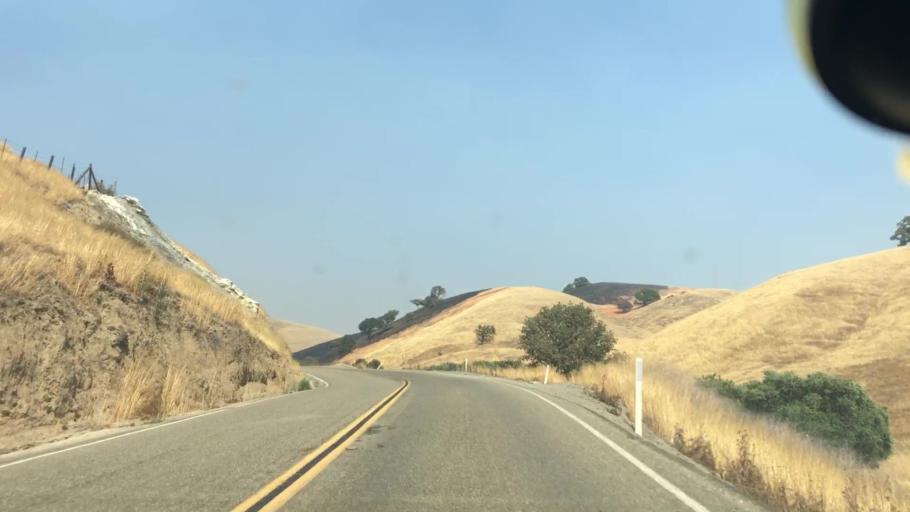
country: US
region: California
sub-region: Alameda County
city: Livermore
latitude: 37.6465
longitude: -121.6225
